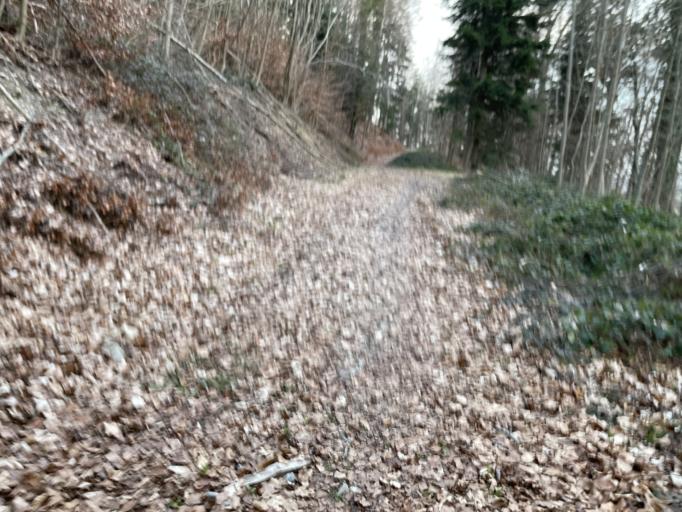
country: CH
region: Bern
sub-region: Bern-Mittelland District
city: Muhlethurnen
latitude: 46.8366
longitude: 7.5314
